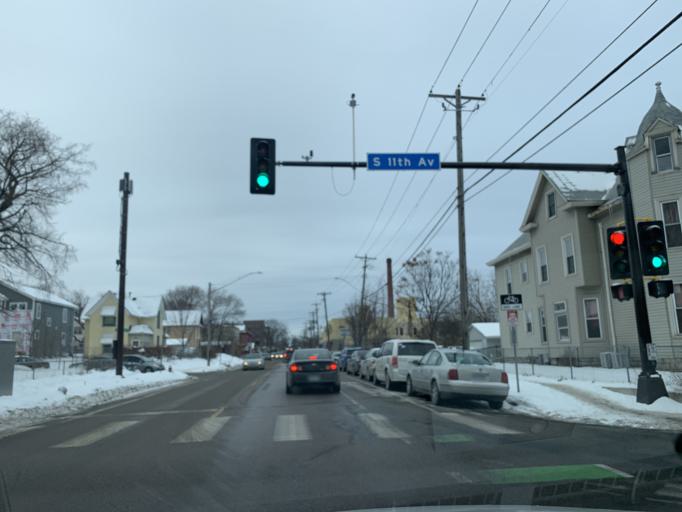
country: US
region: Minnesota
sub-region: Hennepin County
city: Minneapolis
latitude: 44.9592
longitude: -93.2582
